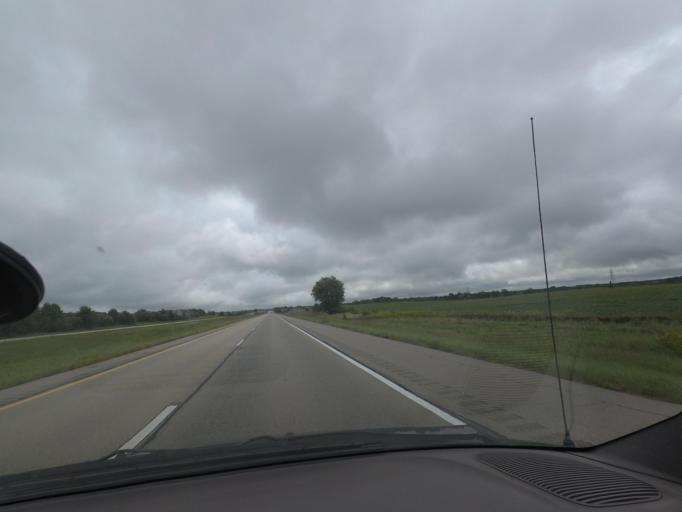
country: US
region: Illinois
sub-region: Piatt County
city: Monticello
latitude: 40.0308
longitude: -88.6300
